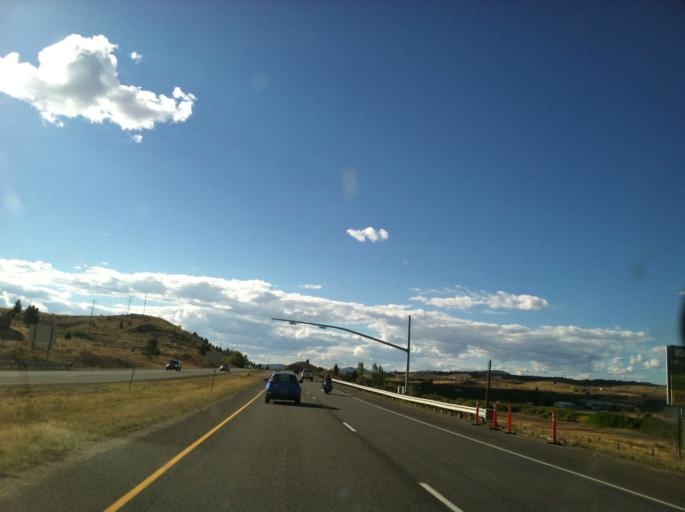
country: US
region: Montana
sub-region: Silver Bow County
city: Butte
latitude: 45.9936
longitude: -112.5576
